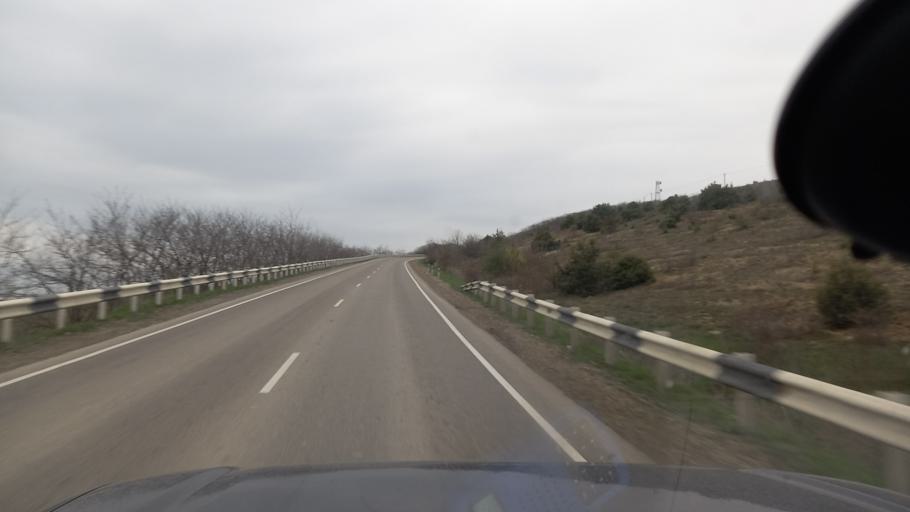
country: RU
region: Krasnodarskiy
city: Sukko
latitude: 44.8391
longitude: 37.4230
